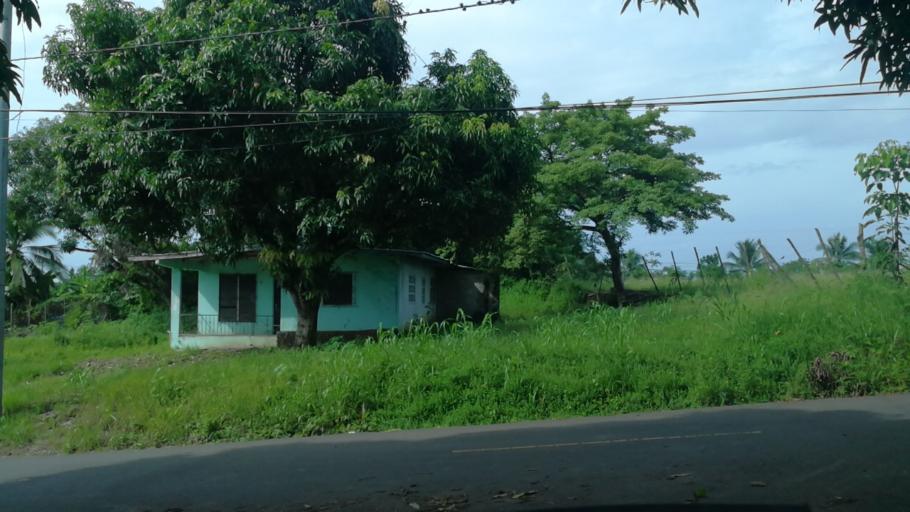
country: PA
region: Panama
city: Pacora
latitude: 9.0819
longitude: -79.2948
